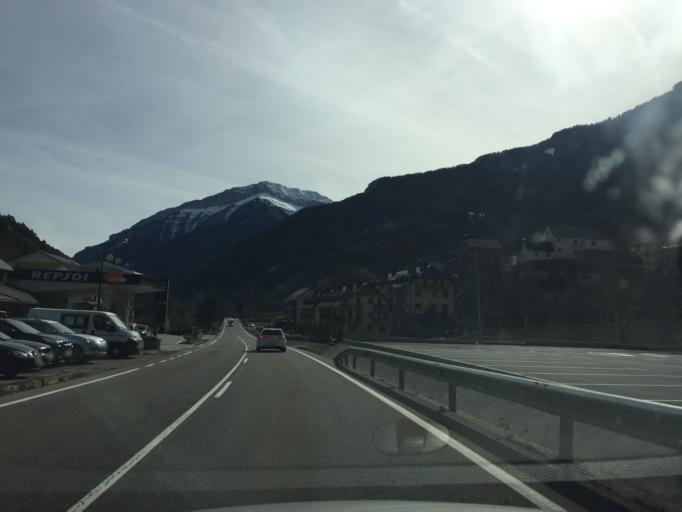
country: ES
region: Aragon
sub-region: Provincia de Huesca
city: Bielsa
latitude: 42.6619
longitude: 0.2093
